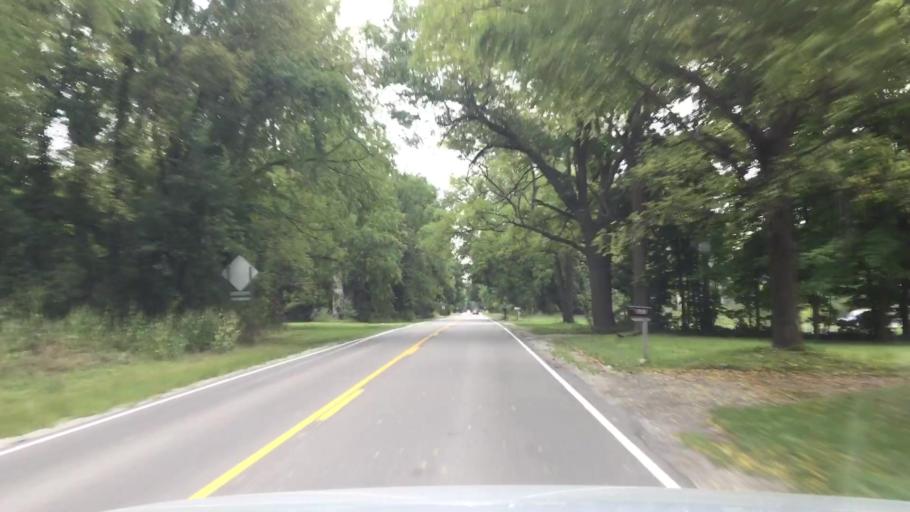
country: US
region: Michigan
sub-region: Washtenaw County
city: Ypsilanti
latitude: 42.1886
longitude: -83.6349
